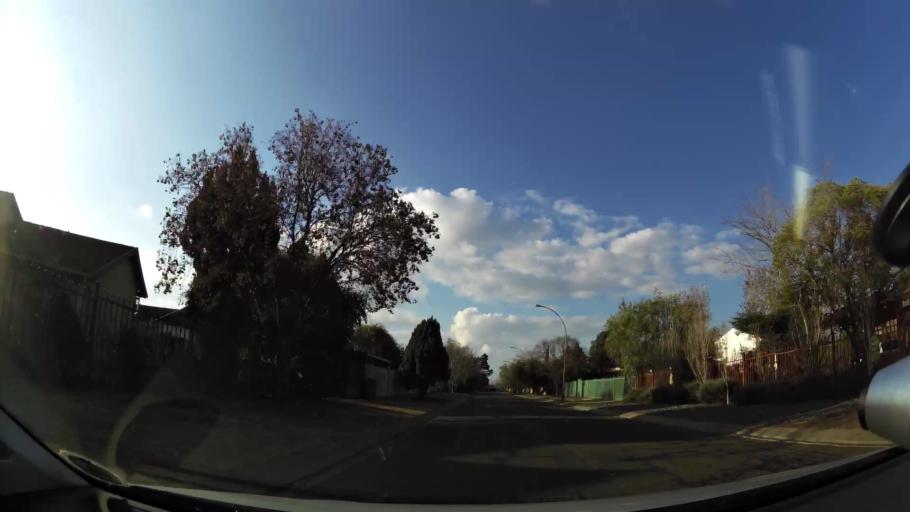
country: ZA
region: Orange Free State
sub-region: Mangaung Metropolitan Municipality
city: Bloemfontein
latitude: -29.1582
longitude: 26.1841
